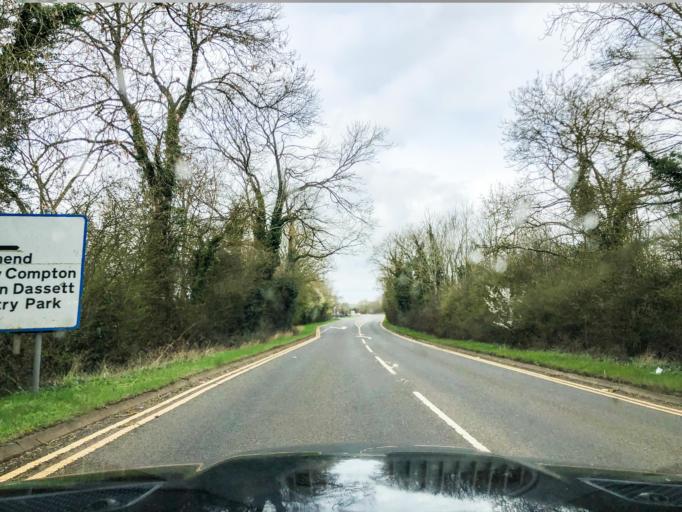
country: GB
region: England
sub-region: Warwickshire
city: Harbury
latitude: 52.1621
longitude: -1.4386
